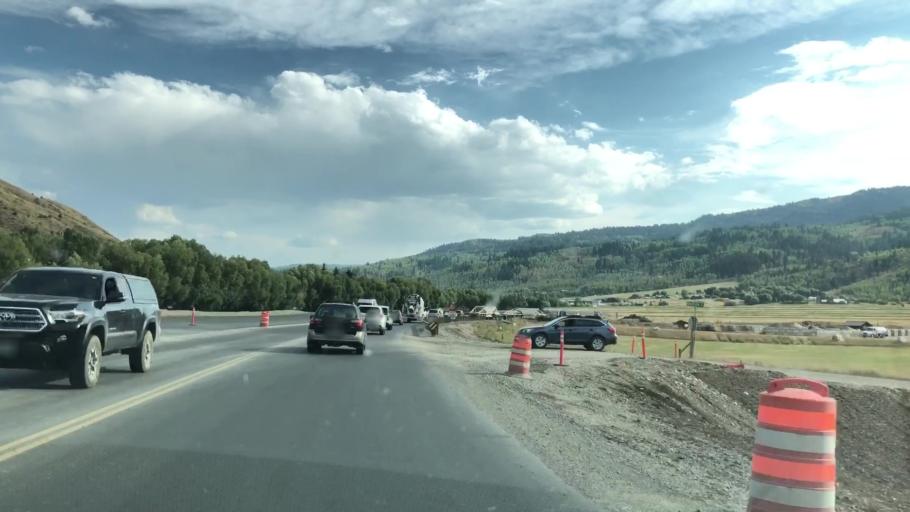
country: US
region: Wyoming
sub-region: Teton County
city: South Park
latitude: 43.3826
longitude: -110.7443
